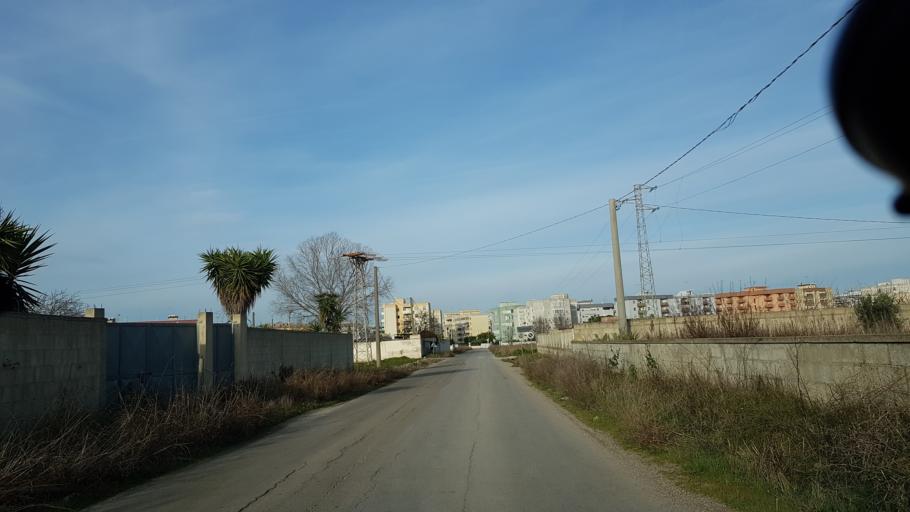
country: IT
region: Apulia
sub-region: Provincia di Brindisi
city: Brindisi
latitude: 40.6147
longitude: 17.9164
